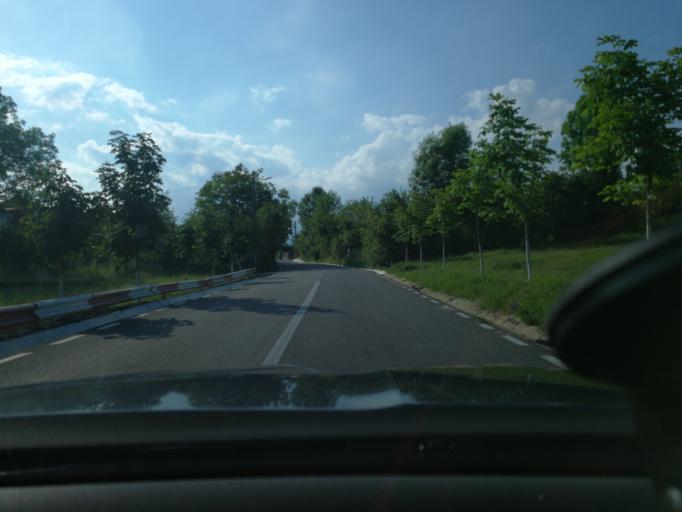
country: RO
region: Prahova
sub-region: Comuna Cornu
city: Cornu de Jos
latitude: 45.1506
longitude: 25.7228
